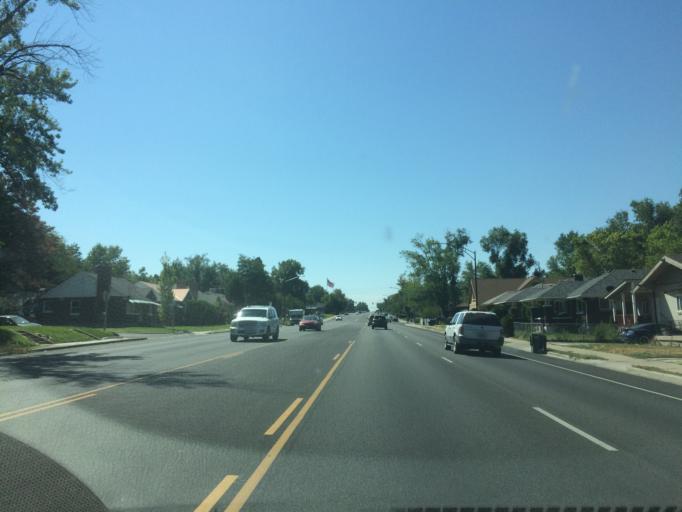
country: US
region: Utah
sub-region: Weber County
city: Ogden
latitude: 41.2178
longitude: -111.9484
